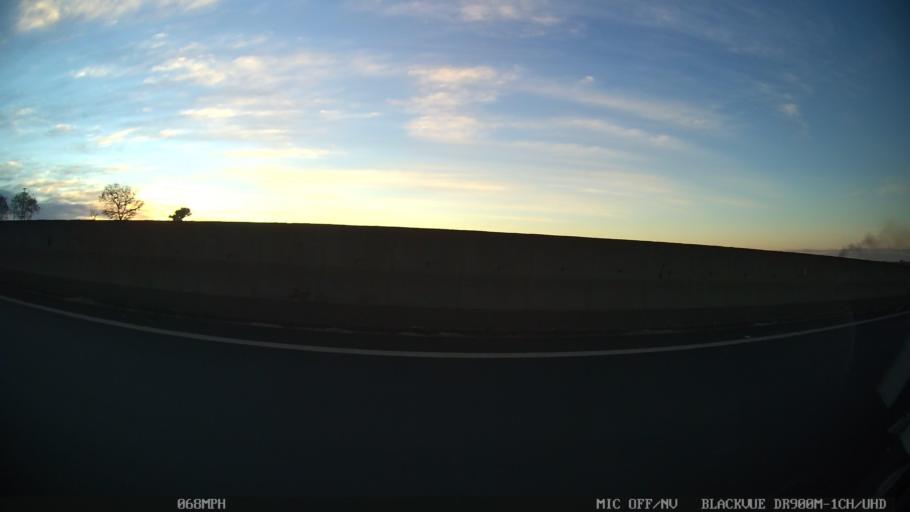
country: BR
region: Sao Paulo
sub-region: Catanduva
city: Catanduva
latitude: -21.1236
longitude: -48.9971
